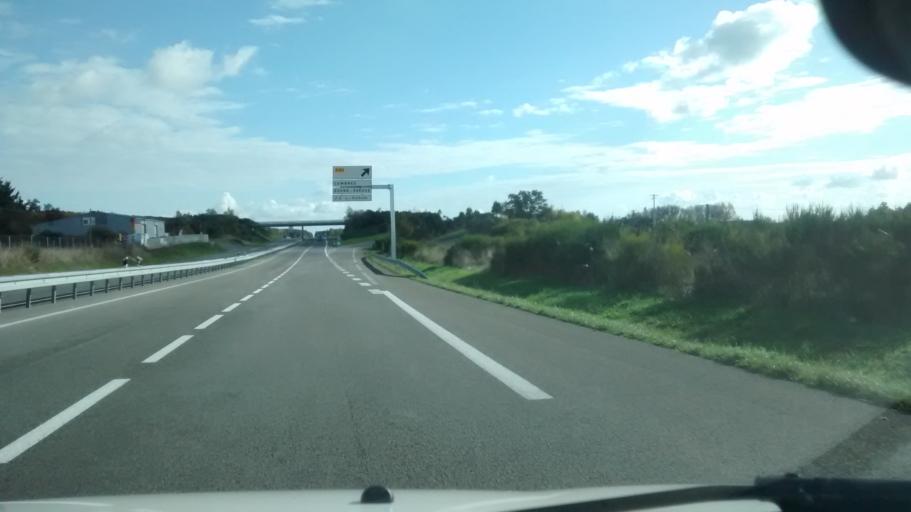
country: FR
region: Pays de la Loire
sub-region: Departement de Maine-et-Loire
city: Combree
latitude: 47.7193
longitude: -1.0328
